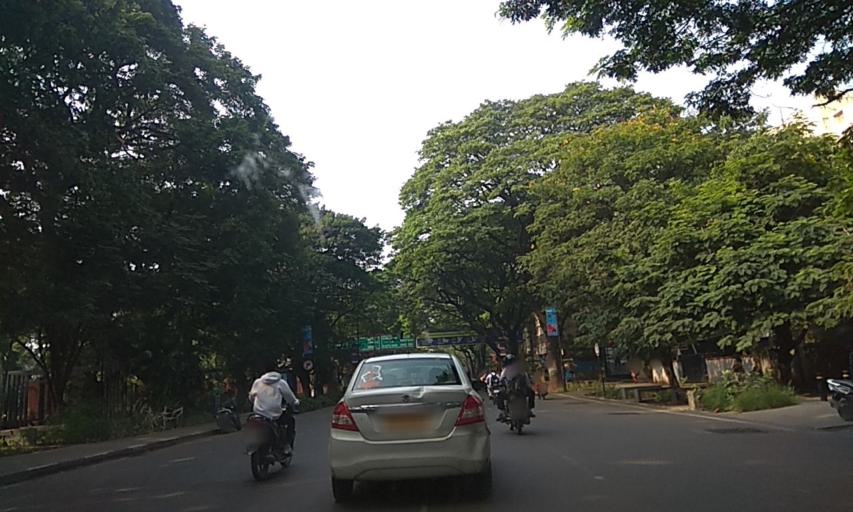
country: IN
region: Maharashtra
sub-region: Pune Division
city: Pune
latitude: 18.5212
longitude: 73.8468
